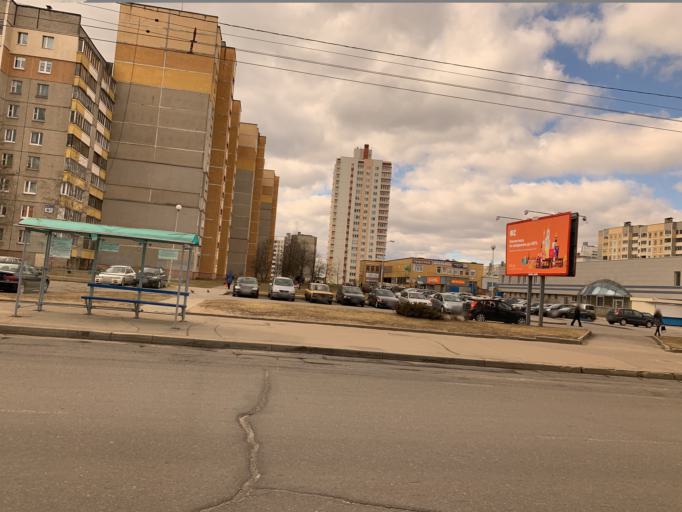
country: BY
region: Minsk
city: Borovlyany
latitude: 53.9380
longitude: 27.6873
